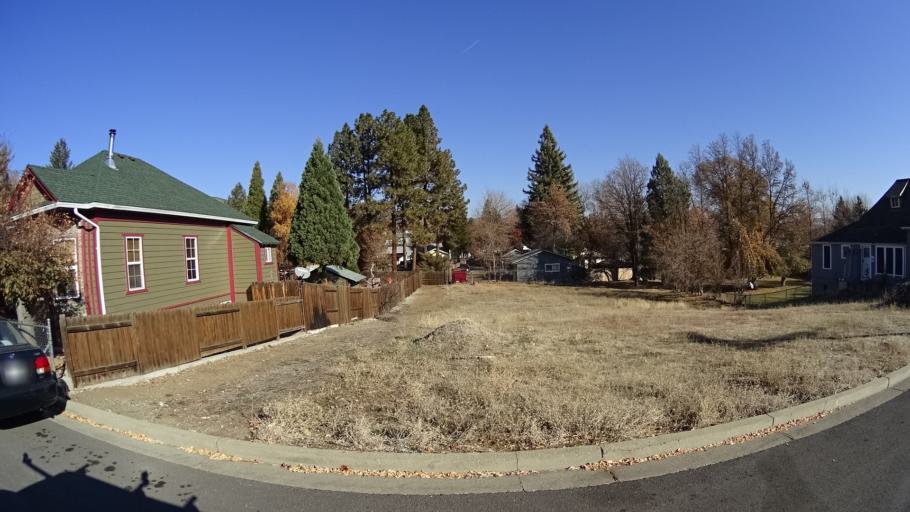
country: US
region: California
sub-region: Siskiyou County
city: Yreka
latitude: 41.7341
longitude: -122.6436
